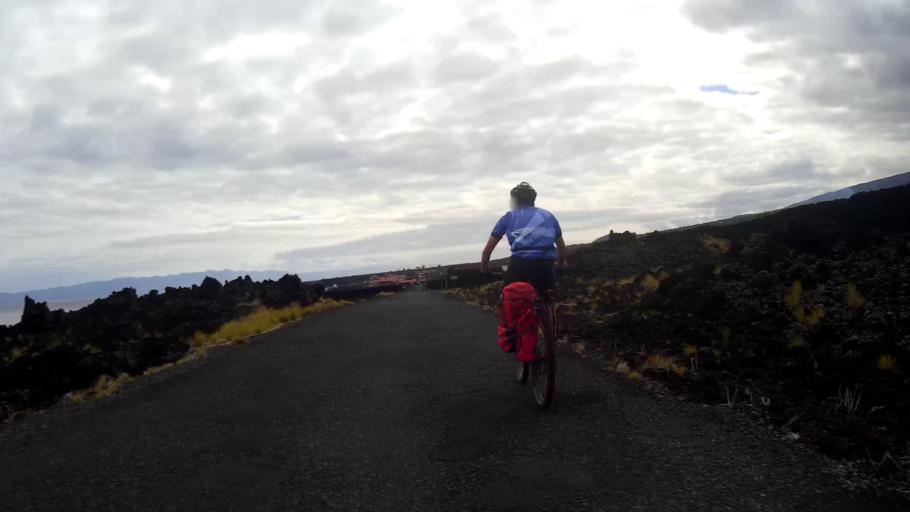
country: PT
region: Azores
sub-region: Madalena
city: Madalena
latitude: 38.5570
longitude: -28.4347
